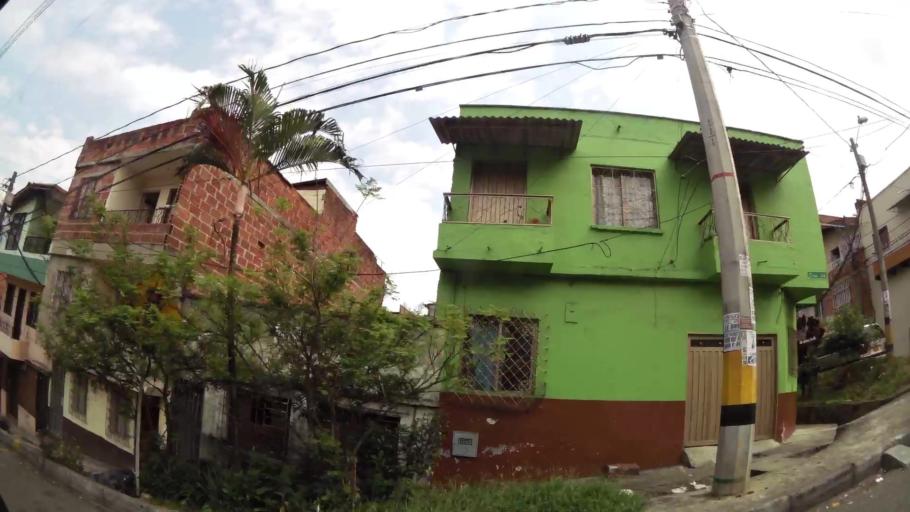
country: CO
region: Antioquia
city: Medellin
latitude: 6.2761
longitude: -75.5530
